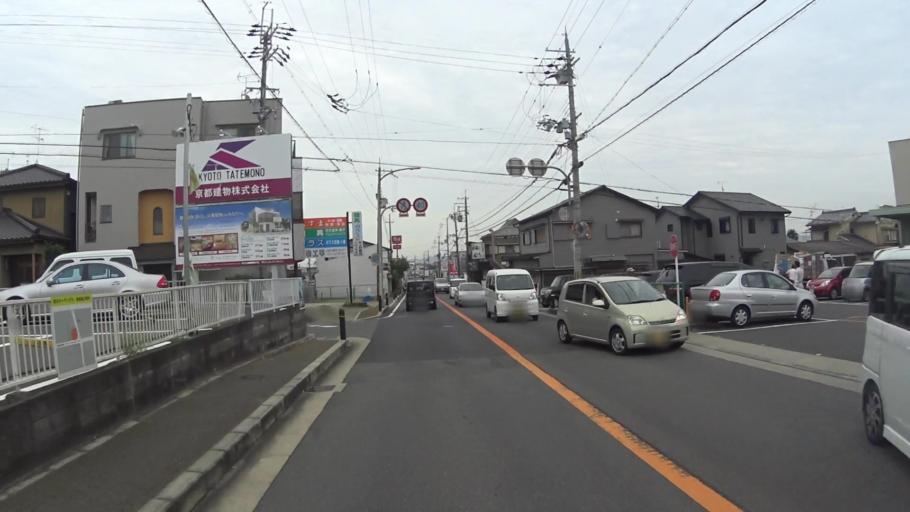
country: JP
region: Kyoto
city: Uji
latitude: 34.8612
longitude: 135.7767
